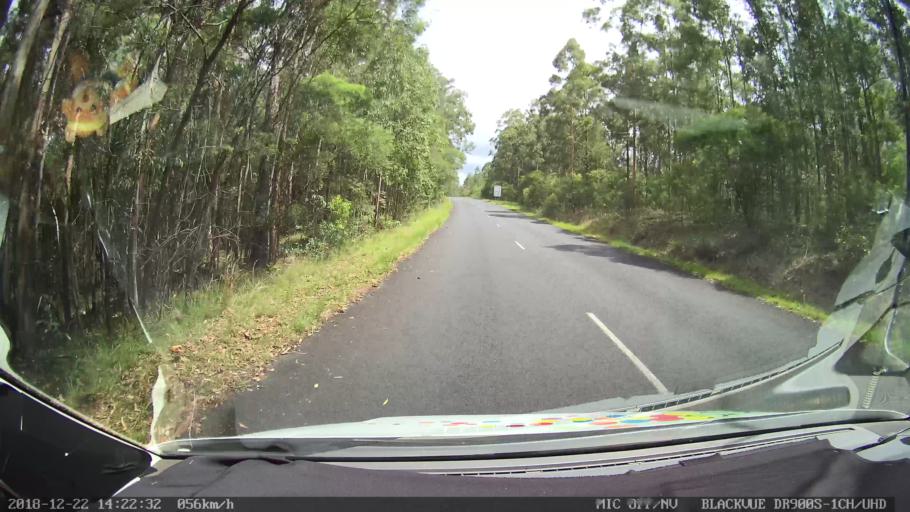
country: AU
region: New South Wales
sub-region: Clarence Valley
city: Coutts Crossing
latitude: -30.0267
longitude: 152.6535
